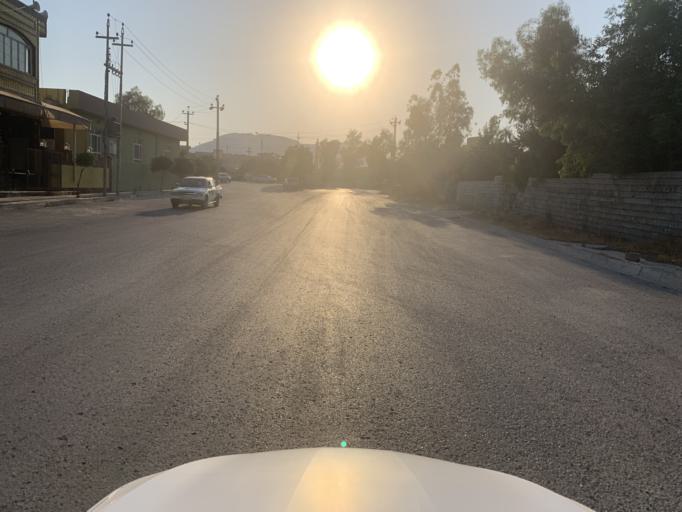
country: IQ
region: As Sulaymaniyah
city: Raniye
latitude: 36.2458
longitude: 44.8830
